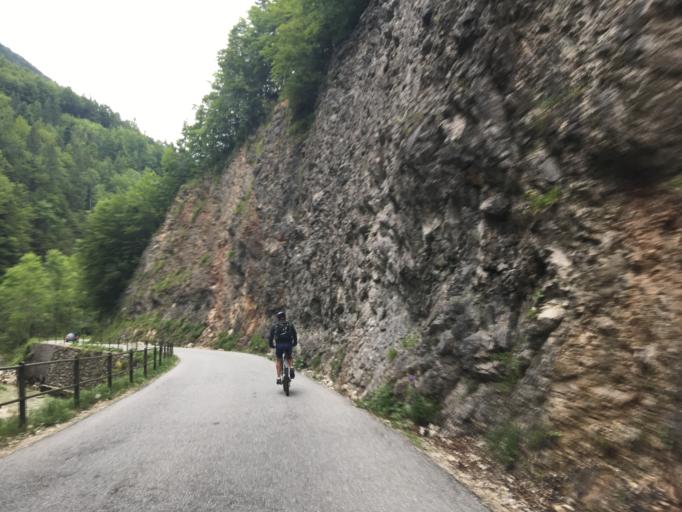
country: AT
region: Salzburg
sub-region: Politischer Bezirk Salzburg-Umgebung
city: Strobl
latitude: 47.6870
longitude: 13.4834
